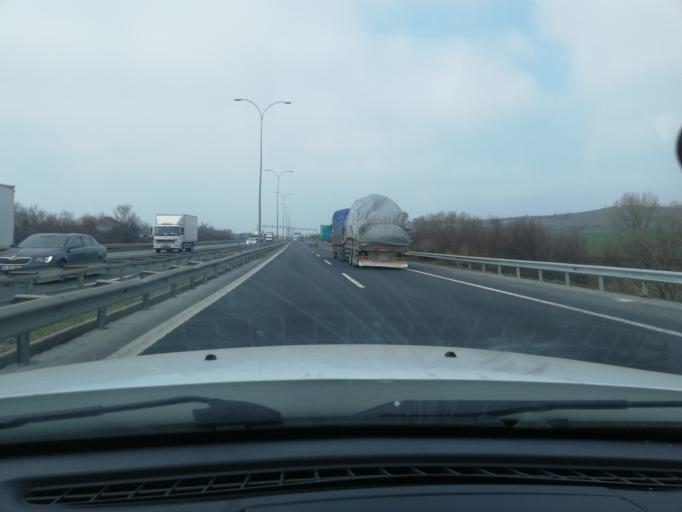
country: TR
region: Istanbul
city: Celaliye
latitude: 41.0660
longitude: 28.3995
